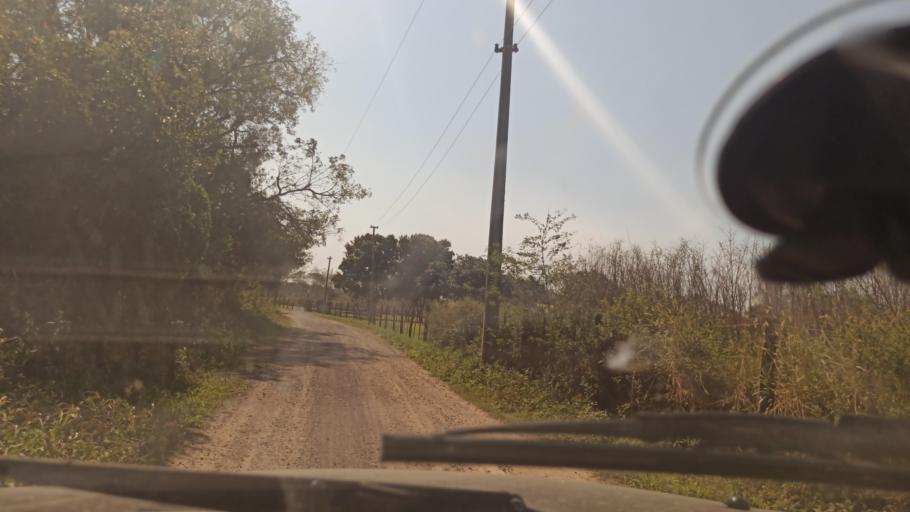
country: AR
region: Formosa
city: Clorinda
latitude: -25.3260
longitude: -57.6918
